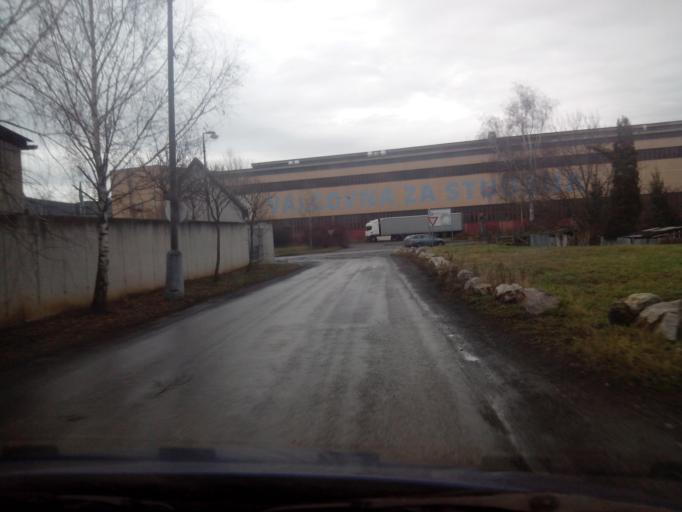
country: CZ
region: Central Bohemia
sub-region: Okres Beroun
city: Kraluv Dvur
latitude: 49.9373
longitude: 14.0309
